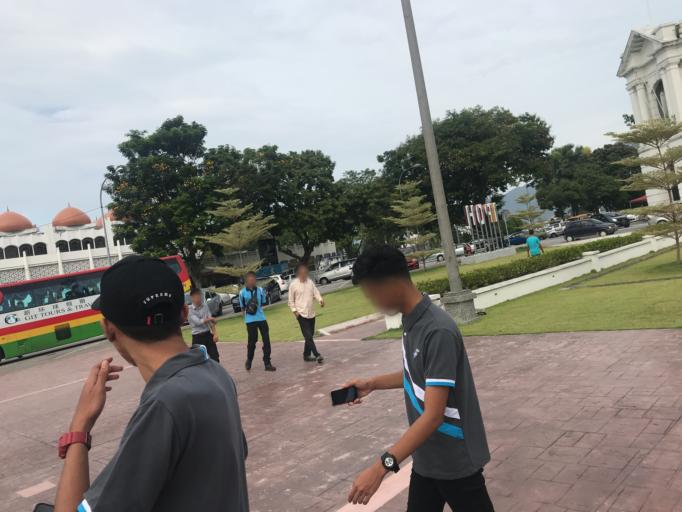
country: MY
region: Perak
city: Ipoh
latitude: 4.5969
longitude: 101.0759
